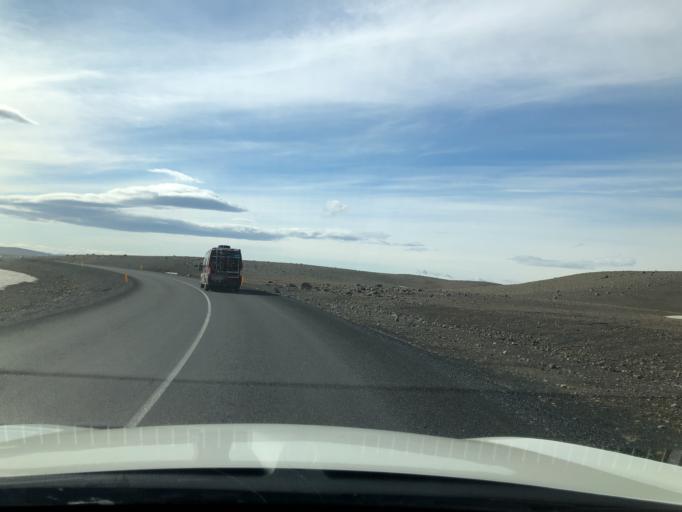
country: IS
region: Northeast
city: Husavik
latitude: 65.8134
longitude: -16.4088
